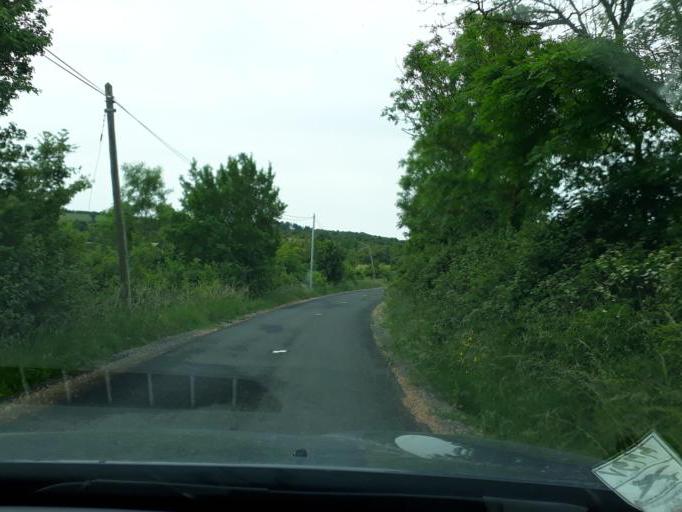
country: FR
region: Languedoc-Roussillon
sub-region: Departement de l'Herault
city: Lodeve
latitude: 43.8376
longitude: 3.2782
